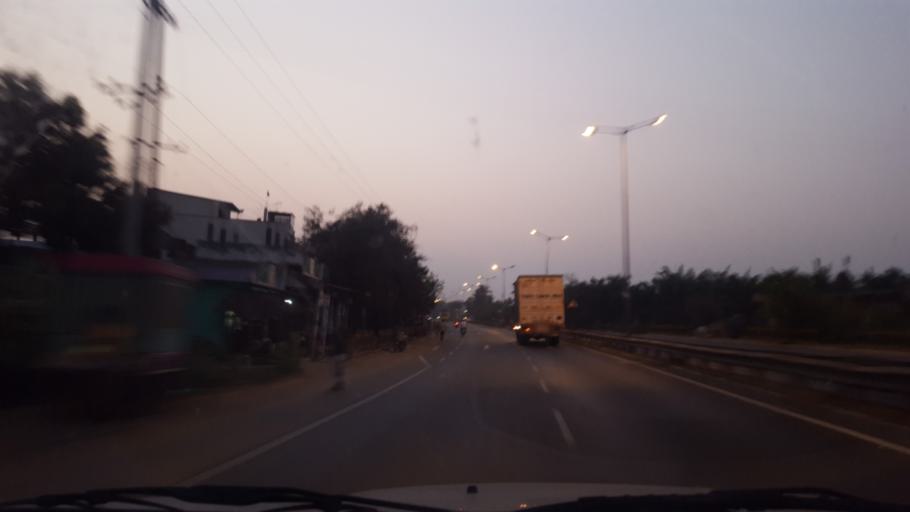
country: IN
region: Andhra Pradesh
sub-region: East Godavari
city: Peddapuram
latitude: 17.1575
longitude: 81.9981
